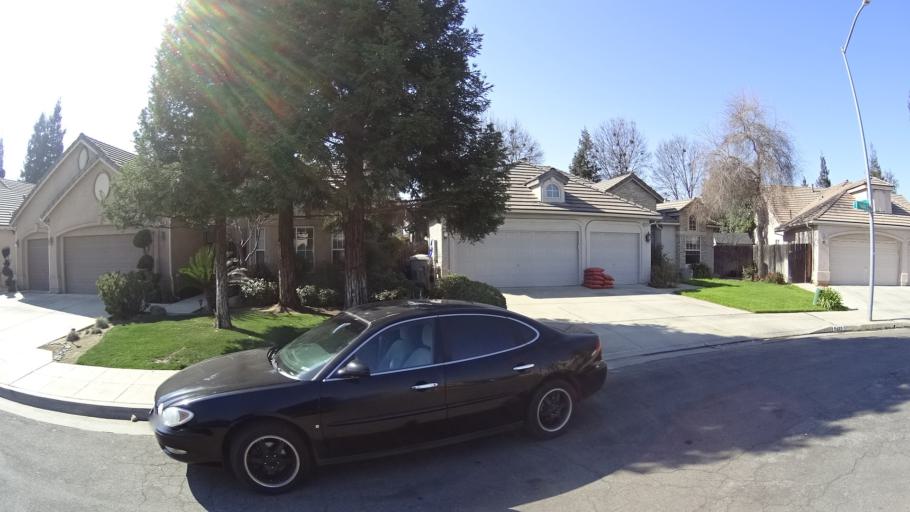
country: US
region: California
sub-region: Fresno County
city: Clovis
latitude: 36.8734
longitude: -119.7339
